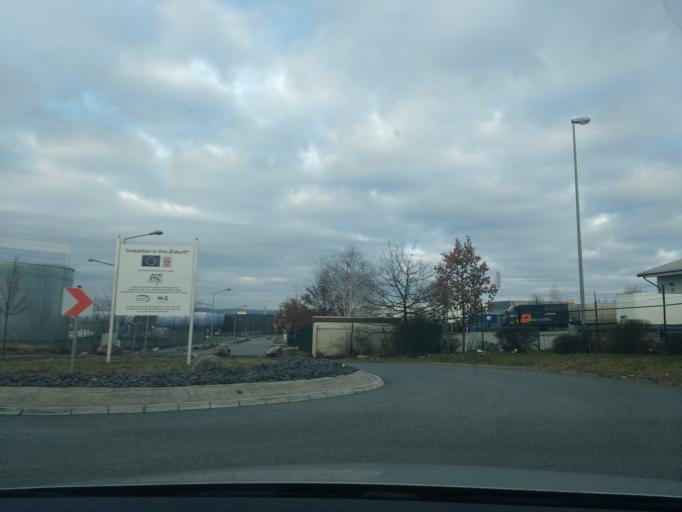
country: DE
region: Hesse
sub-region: Regierungsbezirk Kassel
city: Lohfelden
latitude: 51.2700
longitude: 9.5159
